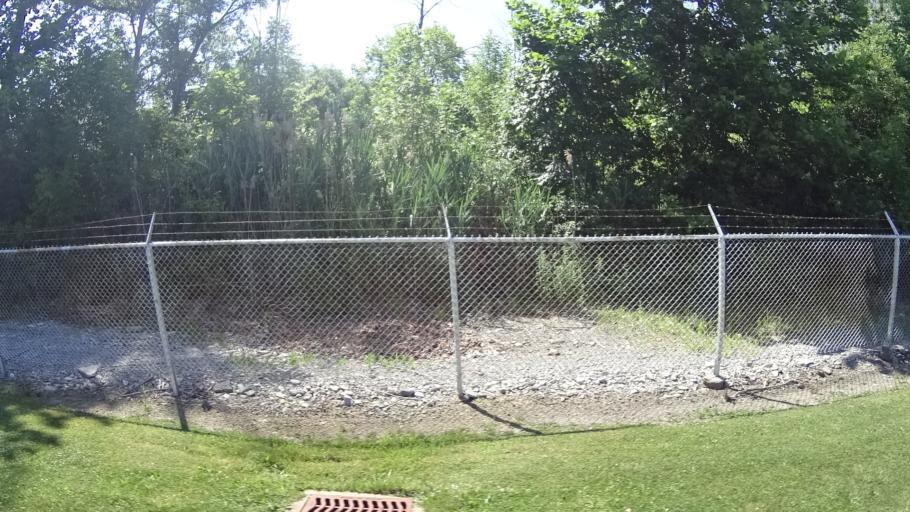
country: US
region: Ohio
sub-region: Erie County
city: Sandusky
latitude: 41.4170
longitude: -82.8103
